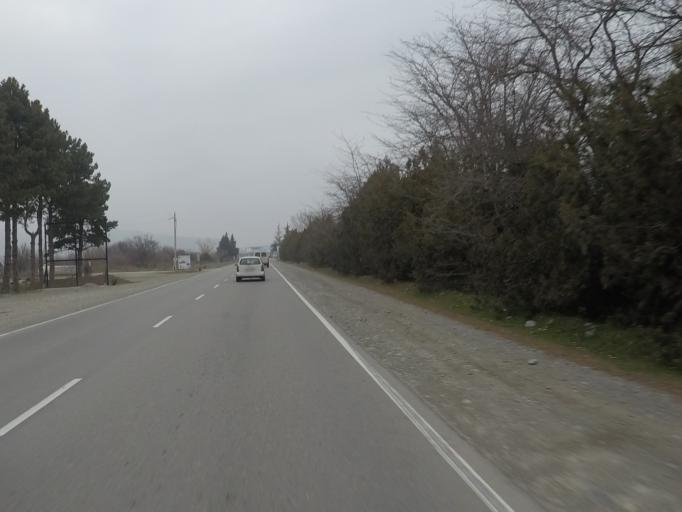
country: GE
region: Mtskheta-Mtianeti
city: Mtskheta
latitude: 41.9088
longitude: 44.7240
